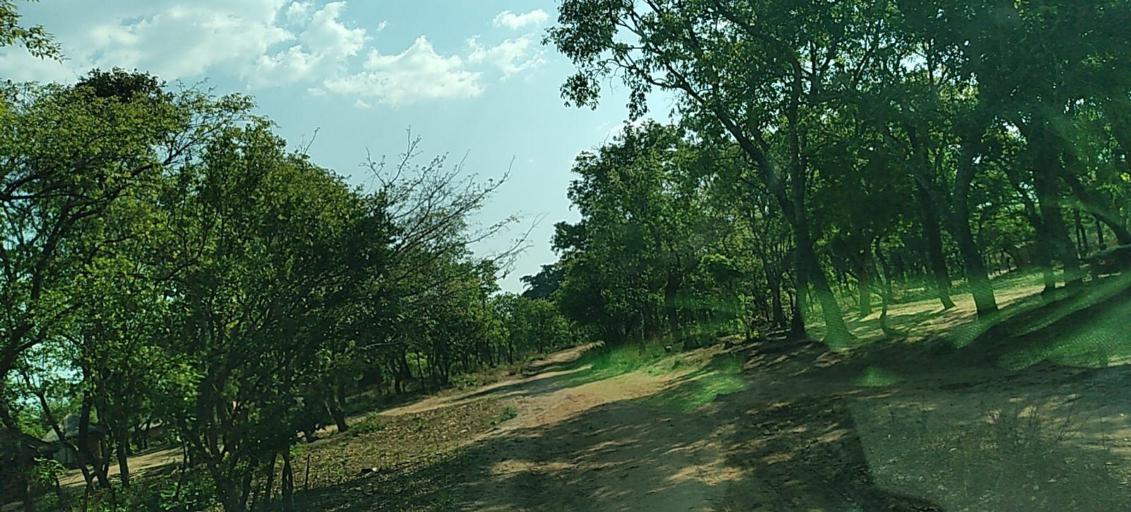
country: ZM
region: North-Western
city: Mwinilunga
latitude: -11.2986
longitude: 24.8538
